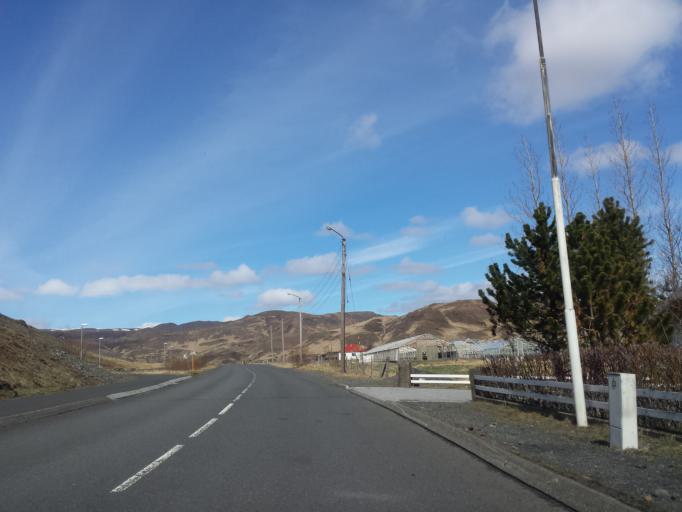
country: IS
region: South
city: Hveragerdi
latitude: 64.0080
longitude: -21.1880
